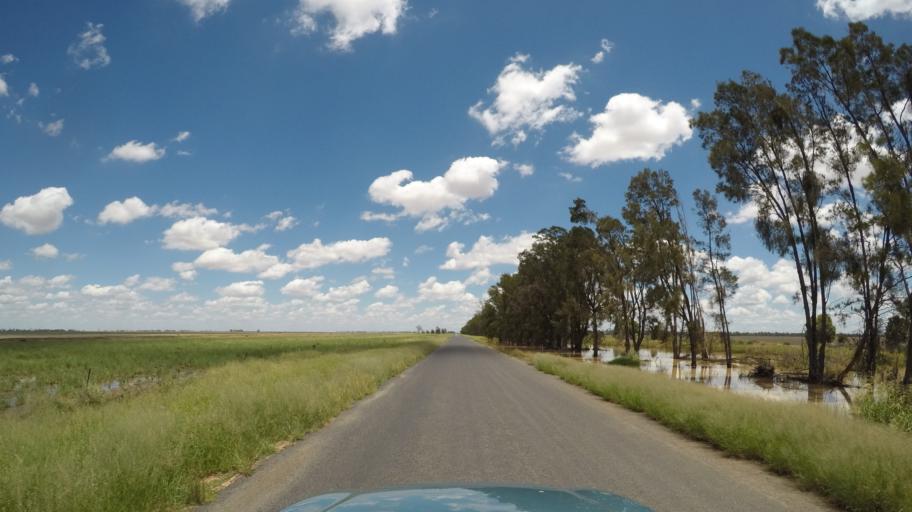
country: AU
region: Queensland
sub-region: Goondiwindi
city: Goondiwindi
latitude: -28.1768
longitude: 150.2631
